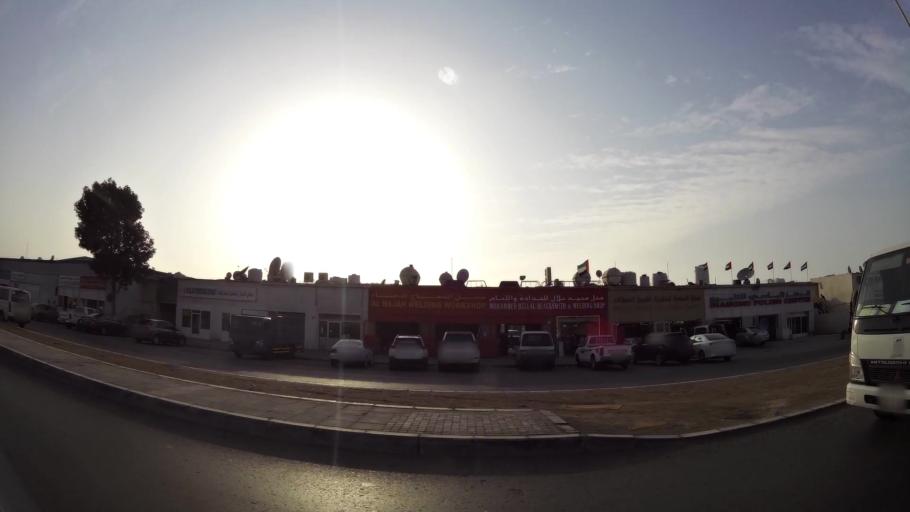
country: AE
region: Abu Dhabi
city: Abu Dhabi
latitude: 24.3785
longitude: 54.5106
